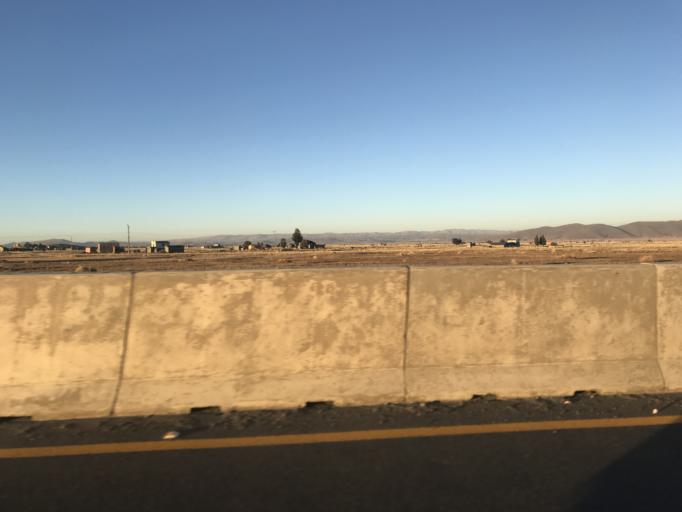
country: BO
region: La Paz
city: Batallas
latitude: -16.3064
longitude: -68.4742
